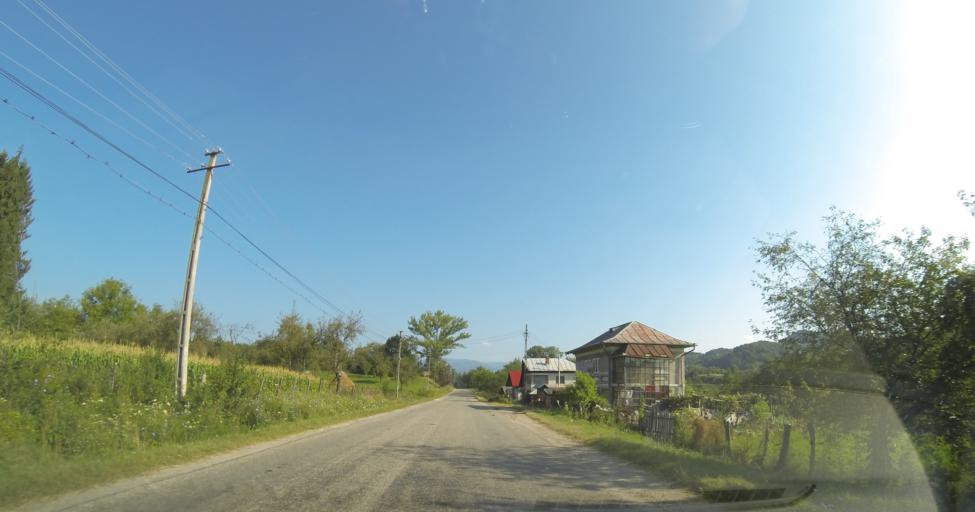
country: RO
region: Valcea
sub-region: Comuna Maldaresti
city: Maldaresti
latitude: 45.1057
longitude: 24.0081
